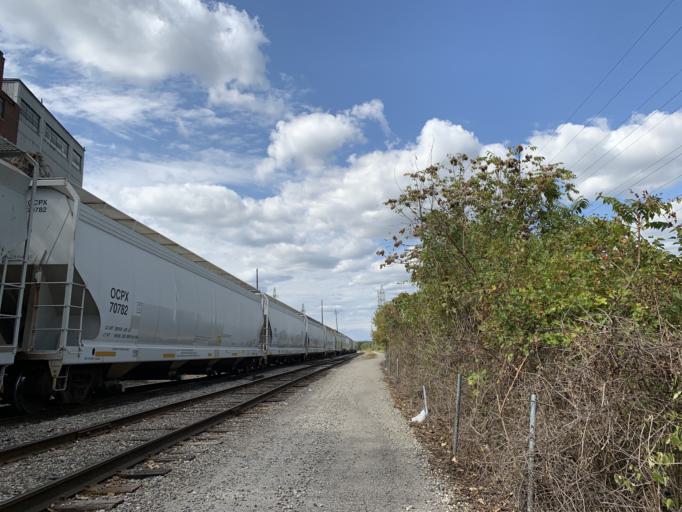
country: US
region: Kentucky
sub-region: Jefferson County
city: Louisville
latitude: 38.2687
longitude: -85.7779
